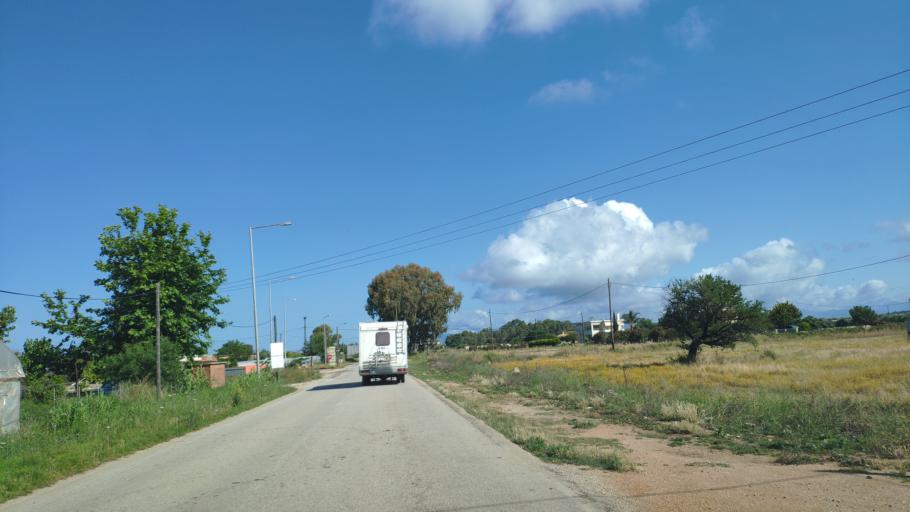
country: GR
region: Epirus
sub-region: Nomos Prevezis
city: Preveza
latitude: 38.9350
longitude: 20.7703
